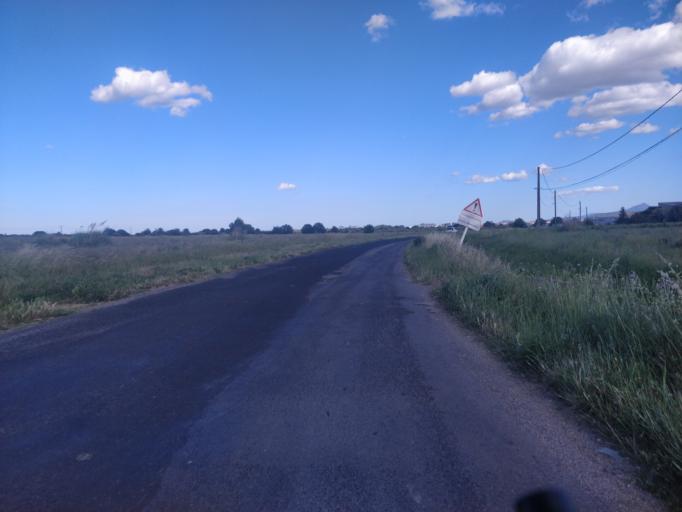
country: FR
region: Languedoc-Roussillon
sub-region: Departement des Pyrenees-Orientales
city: Cabestany
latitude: 42.6727
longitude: 2.9256
